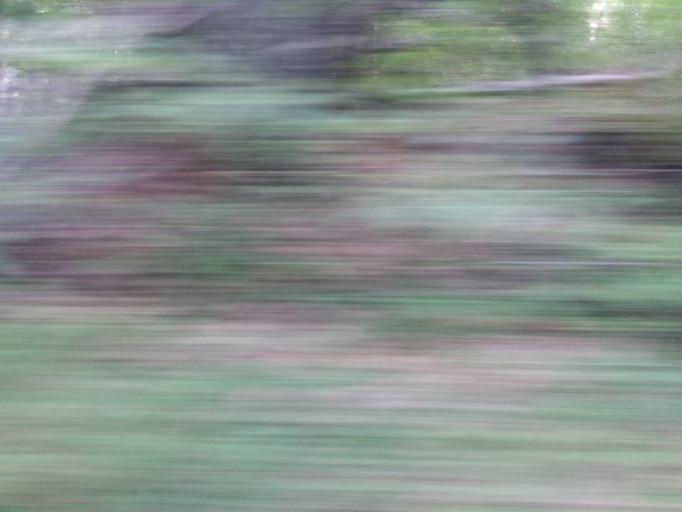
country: US
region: Tennessee
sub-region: Blount County
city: Wildwood
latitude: 35.8634
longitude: -83.8630
